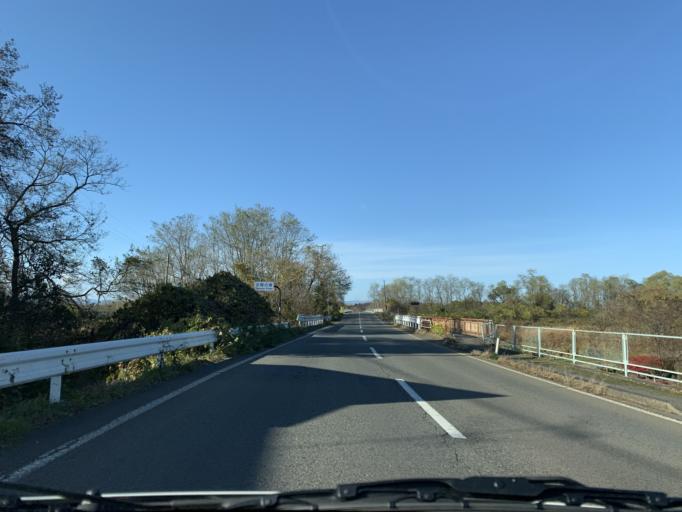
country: JP
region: Iwate
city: Mizusawa
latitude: 39.1841
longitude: 141.1288
